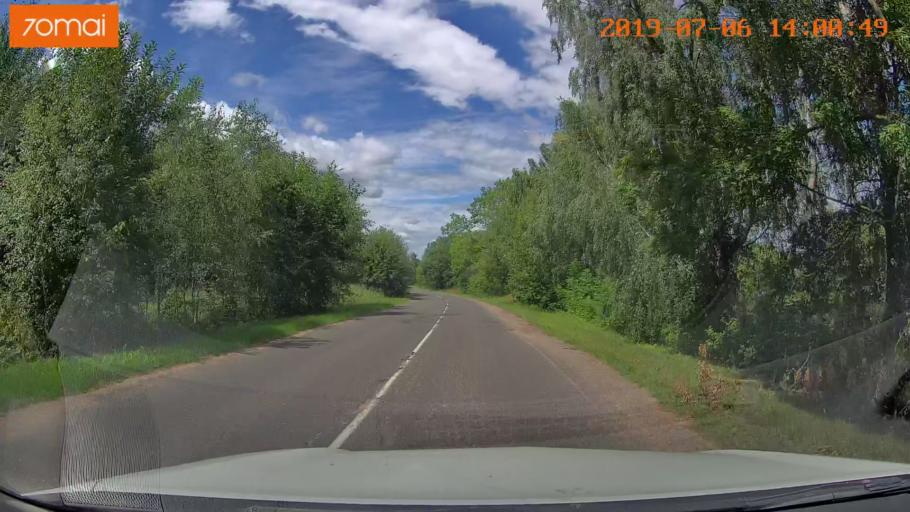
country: BY
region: Minsk
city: Ivyanyets
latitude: 53.8023
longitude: 26.8189
